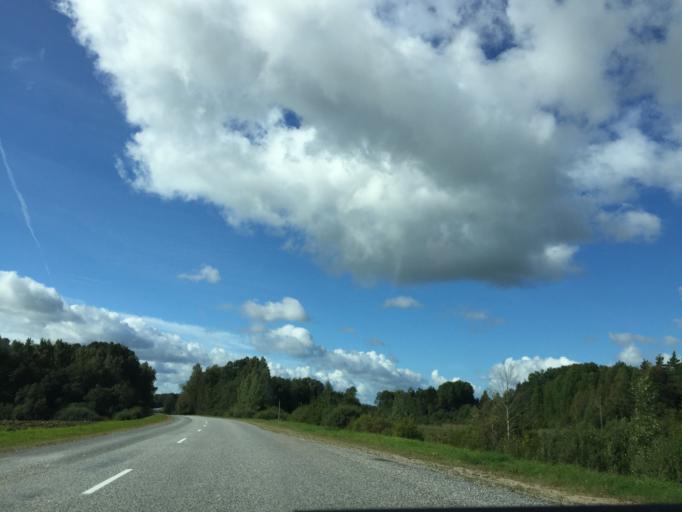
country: LV
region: Kuldigas Rajons
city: Kuldiga
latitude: 56.9921
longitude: 22.0868
